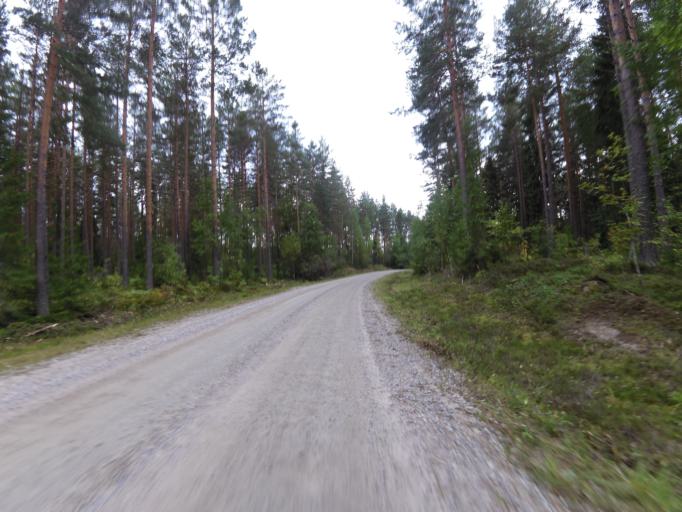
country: SE
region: Gaevleborg
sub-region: Sandvikens Kommun
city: Sandviken
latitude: 60.7589
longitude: 16.8641
